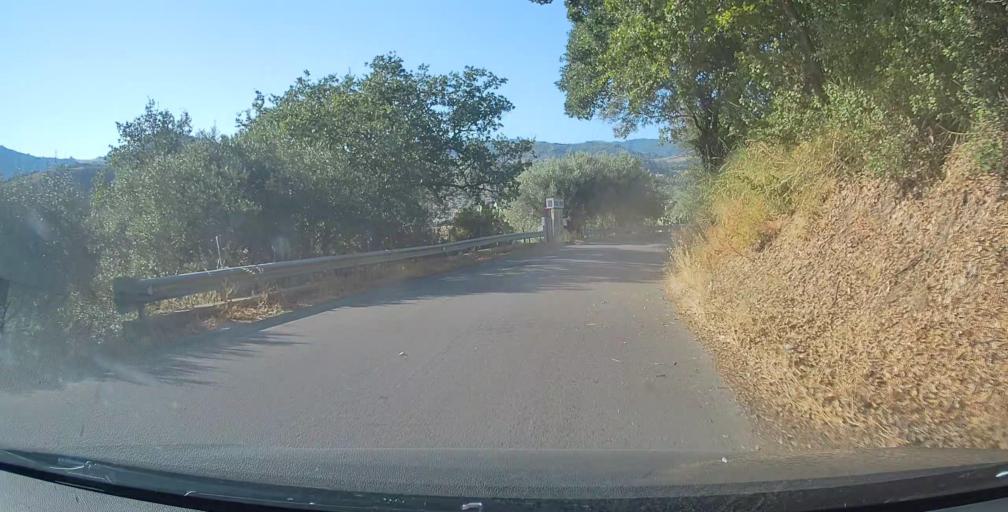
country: IT
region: Sicily
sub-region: Messina
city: Librizzi
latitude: 38.0814
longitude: 14.9747
